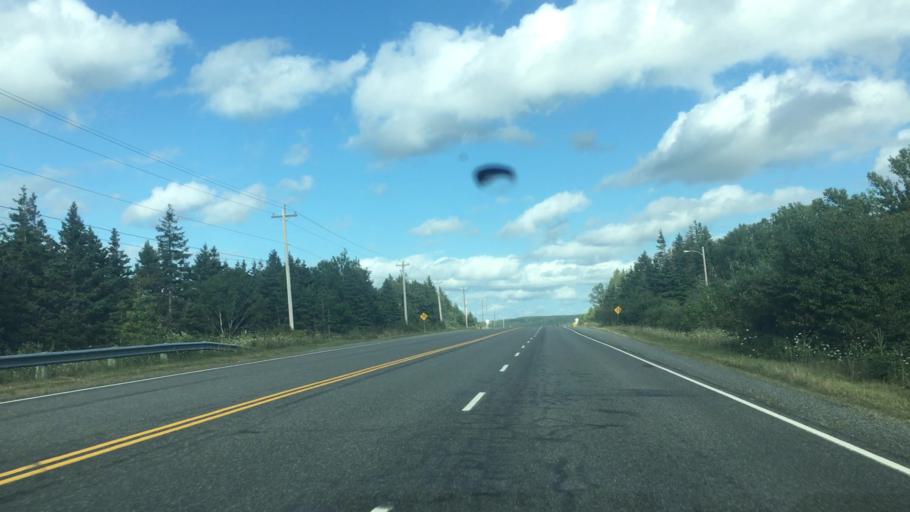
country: CA
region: Nova Scotia
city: Princeville
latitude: 45.8140
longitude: -60.6963
